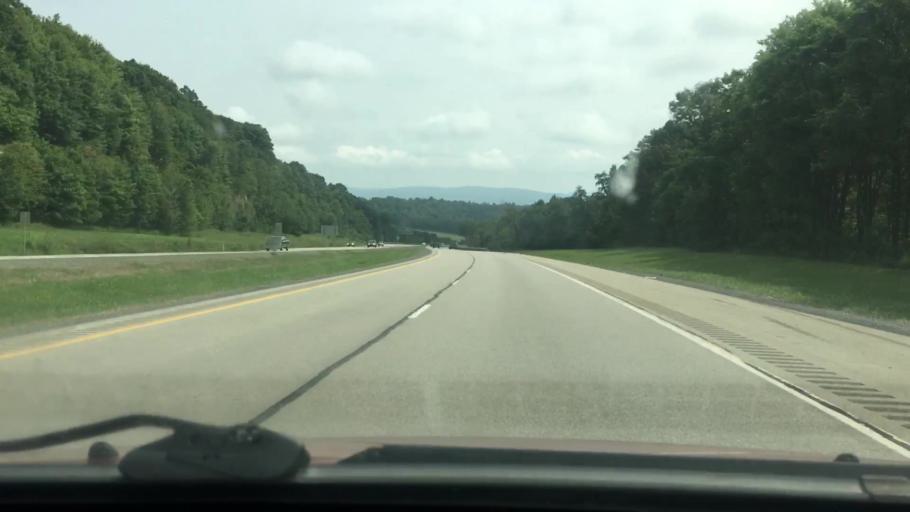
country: US
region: West Virginia
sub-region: Preston County
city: Terra Alta
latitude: 39.6628
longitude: -79.4827
